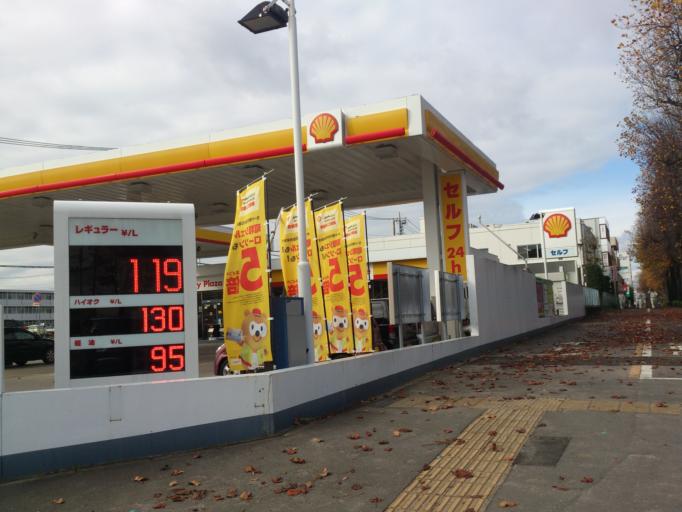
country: JP
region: Ibaraki
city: Naka
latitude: 36.0903
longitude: 140.1010
